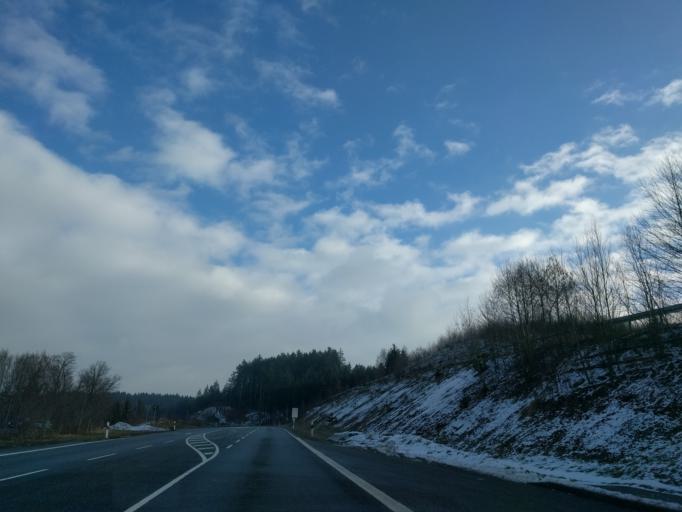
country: DE
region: Bavaria
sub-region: Lower Bavaria
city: Regen
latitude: 48.9784
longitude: 13.1576
